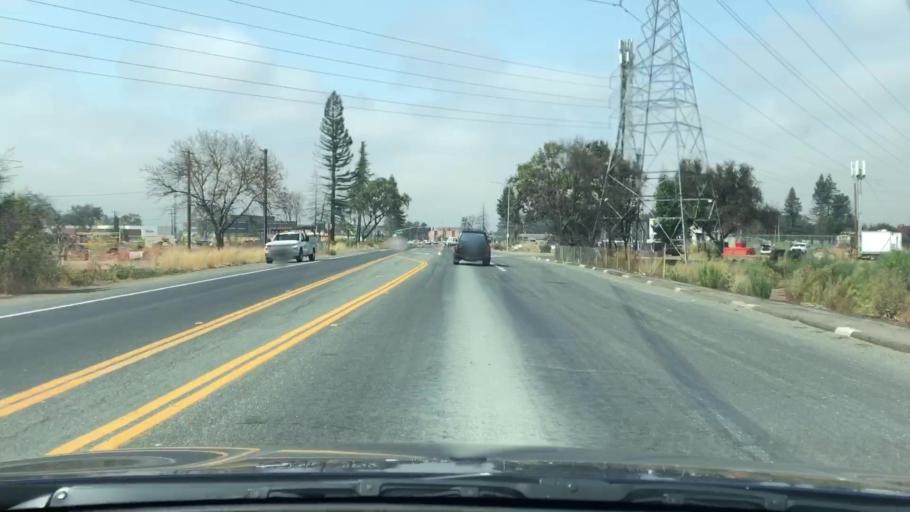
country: US
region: California
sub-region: Sonoma County
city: Larkfield-Wikiup
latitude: 38.4986
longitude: -122.7446
